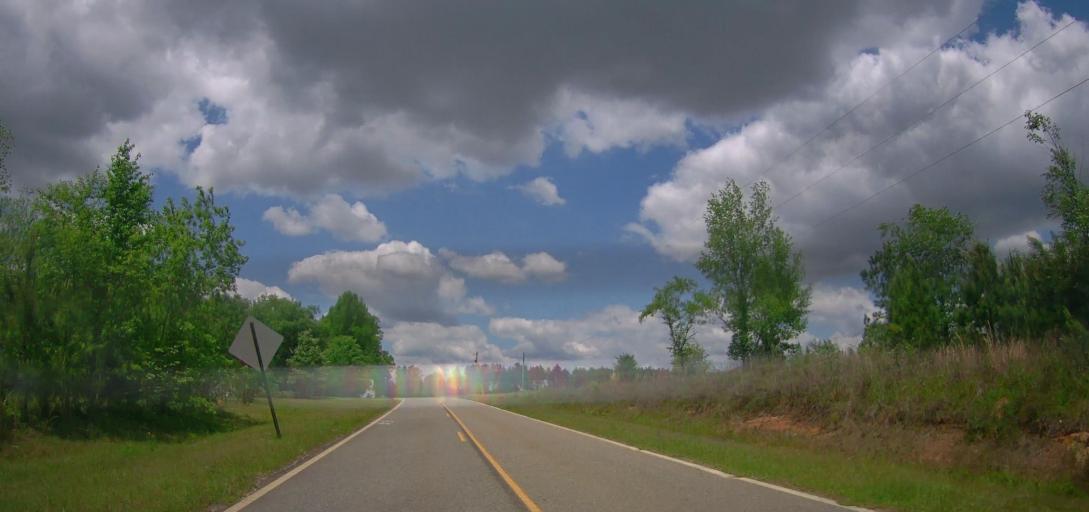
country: US
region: Georgia
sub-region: Laurens County
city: East Dublin
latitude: 32.6016
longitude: -82.8007
